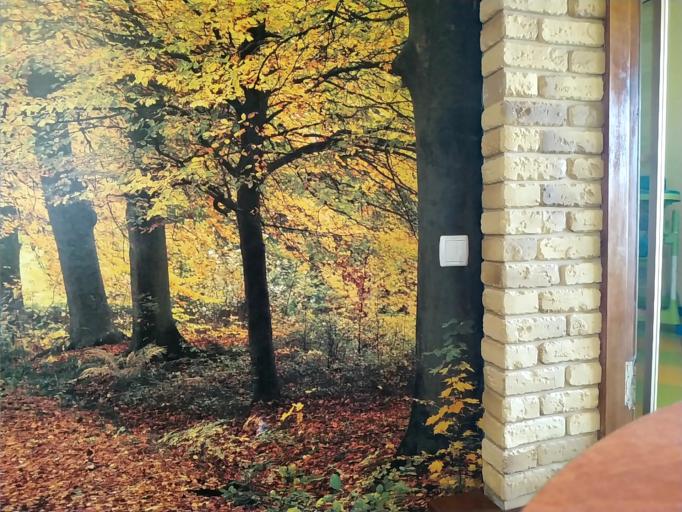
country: RU
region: Tverskaya
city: Maksatikha
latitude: 57.6129
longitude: 35.8380
